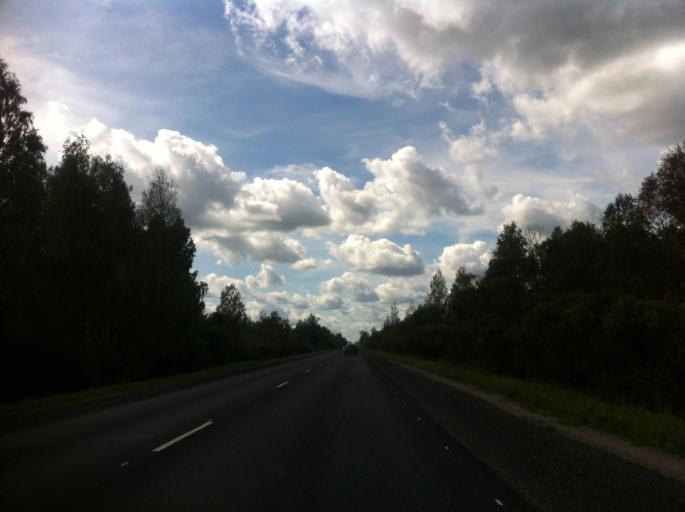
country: RU
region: Pskov
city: Izborsk
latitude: 57.7509
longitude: 28.0512
